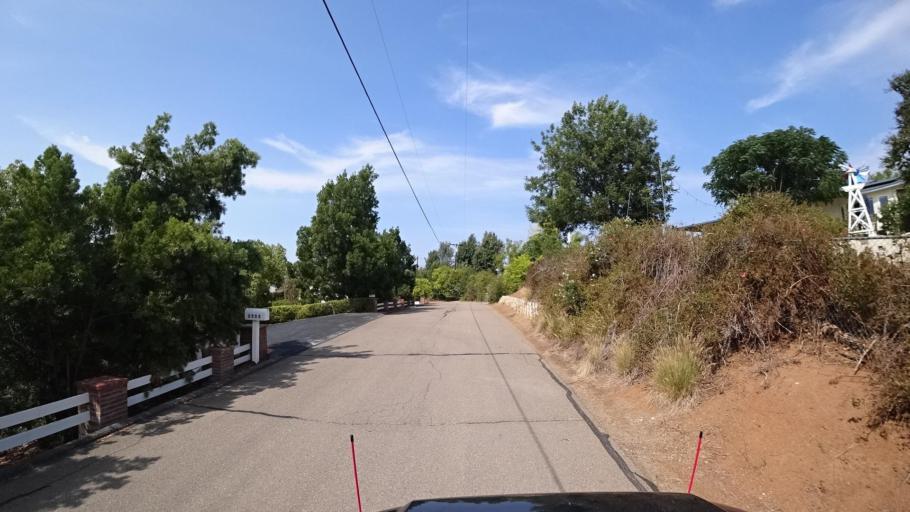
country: US
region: California
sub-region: San Diego County
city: Escondido
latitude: 33.0813
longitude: -117.0492
